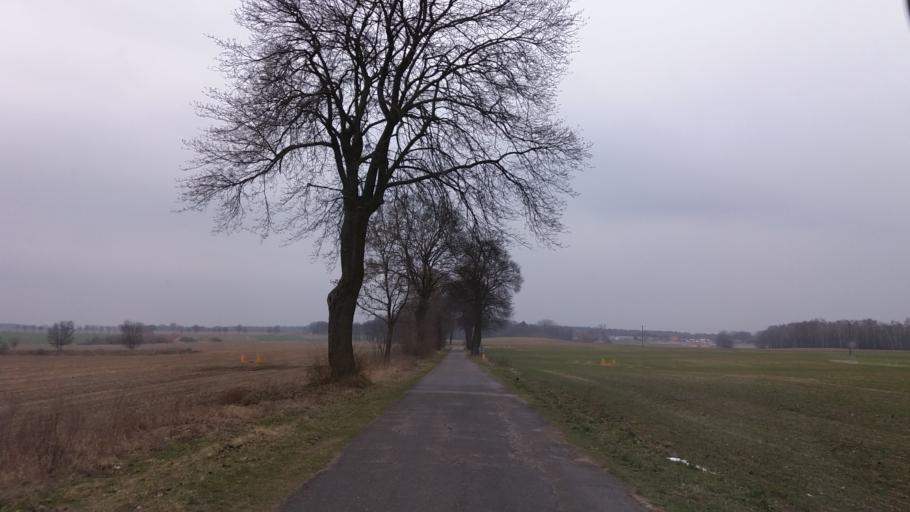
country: PL
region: West Pomeranian Voivodeship
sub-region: Powiat choszczenski
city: Choszczno
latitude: 53.1359
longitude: 15.3623
